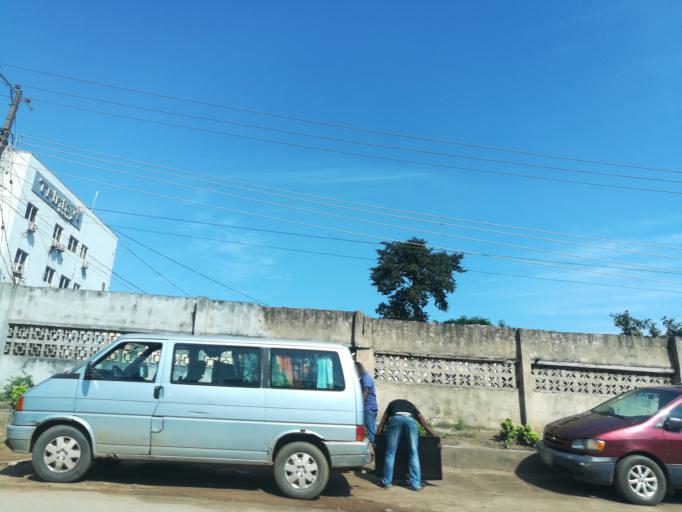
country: NG
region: Lagos
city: Ikeja
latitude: 6.6025
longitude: 3.3444
